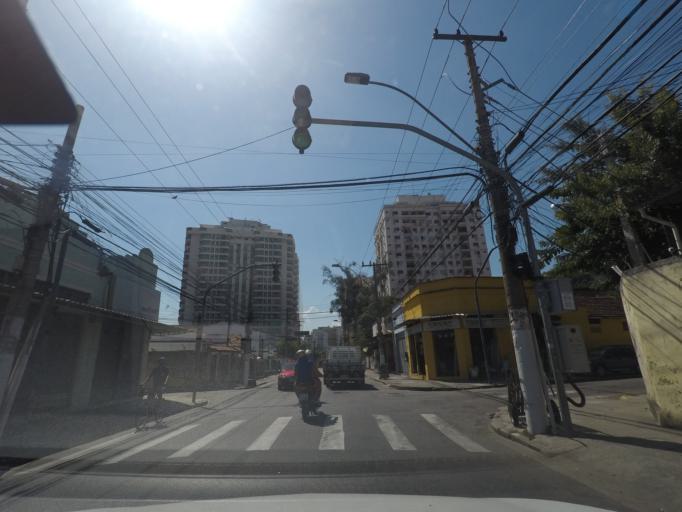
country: BR
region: Rio de Janeiro
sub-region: Niteroi
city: Niteroi
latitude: -22.9049
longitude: -43.0915
